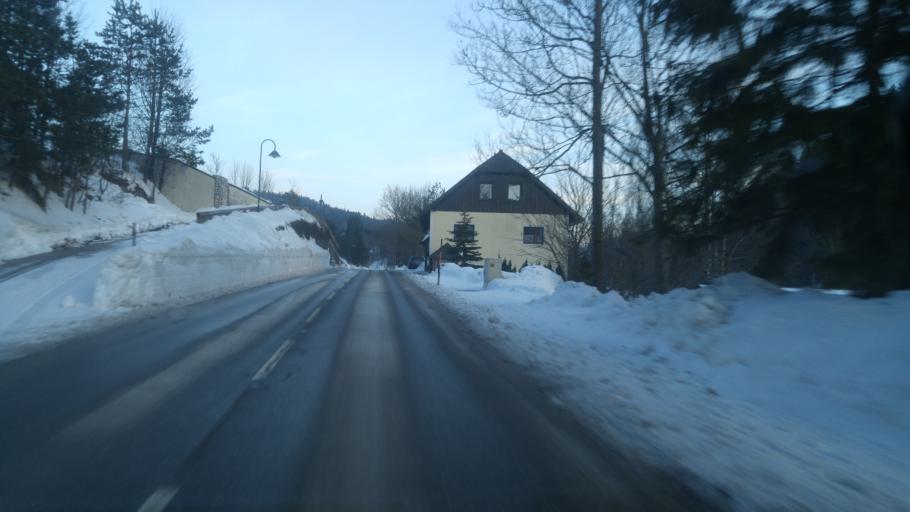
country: AT
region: Lower Austria
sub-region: Politischer Bezirk Wiener Neustadt
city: Rohr im Gebirge
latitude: 47.8947
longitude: 15.7382
